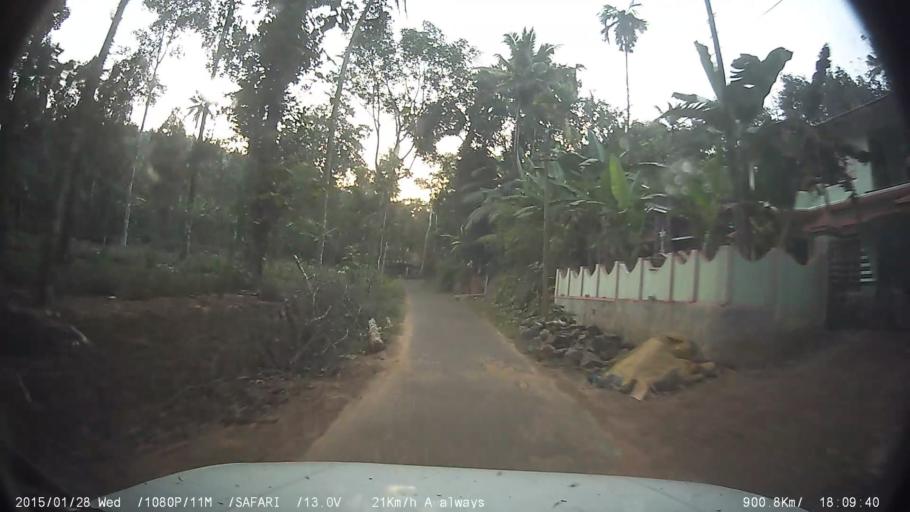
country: IN
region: Kerala
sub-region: Kottayam
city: Palackattumala
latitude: 9.7443
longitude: 76.5732
